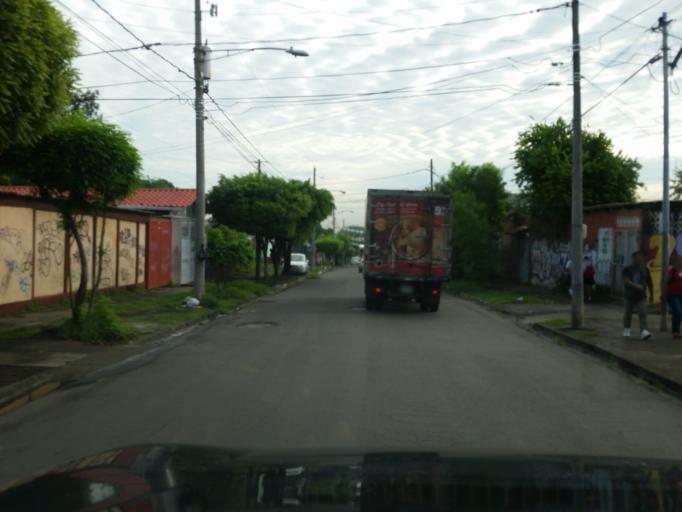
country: NI
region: Managua
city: Managua
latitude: 12.1154
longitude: -86.2026
